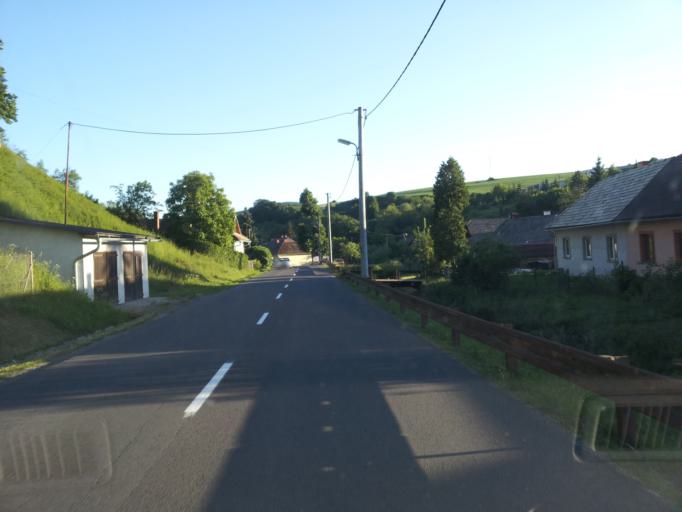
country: SK
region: Banskobystricky
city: Svaety Anton
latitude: 48.4195
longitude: 18.9405
